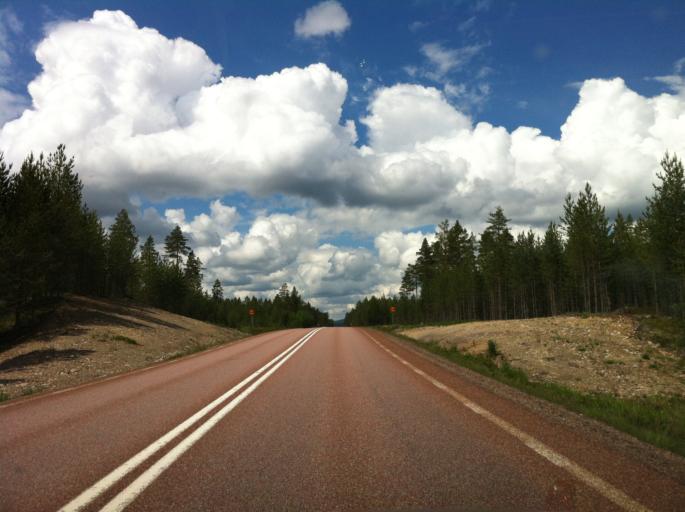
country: SE
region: Dalarna
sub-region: Malung-Saelens kommun
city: Malung
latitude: 60.7826
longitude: 13.4580
